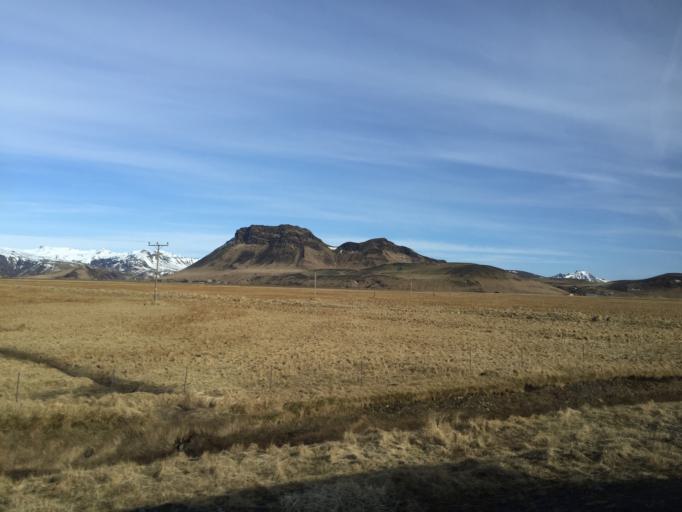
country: IS
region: South
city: Vestmannaeyjar
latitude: 63.4591
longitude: -19.2216
